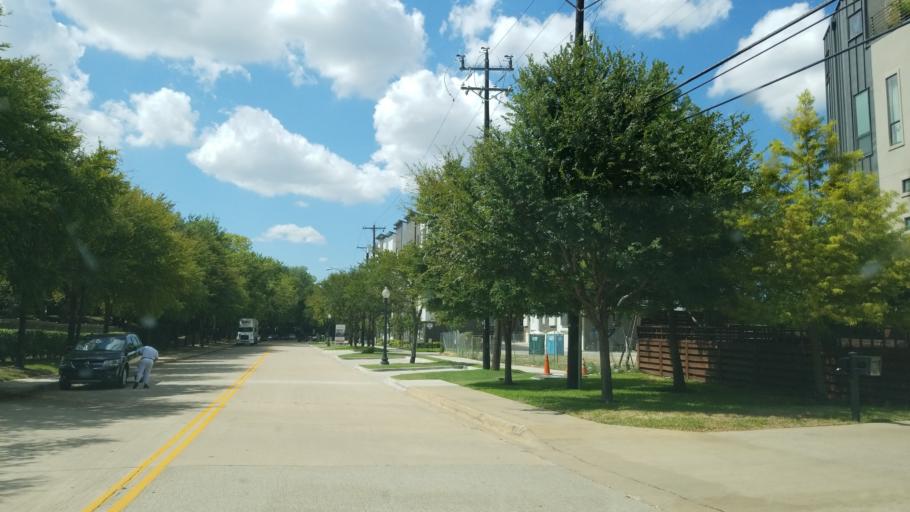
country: US
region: Texas
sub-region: Dallas County
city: Dallas
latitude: 32.7625
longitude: -96.8159
